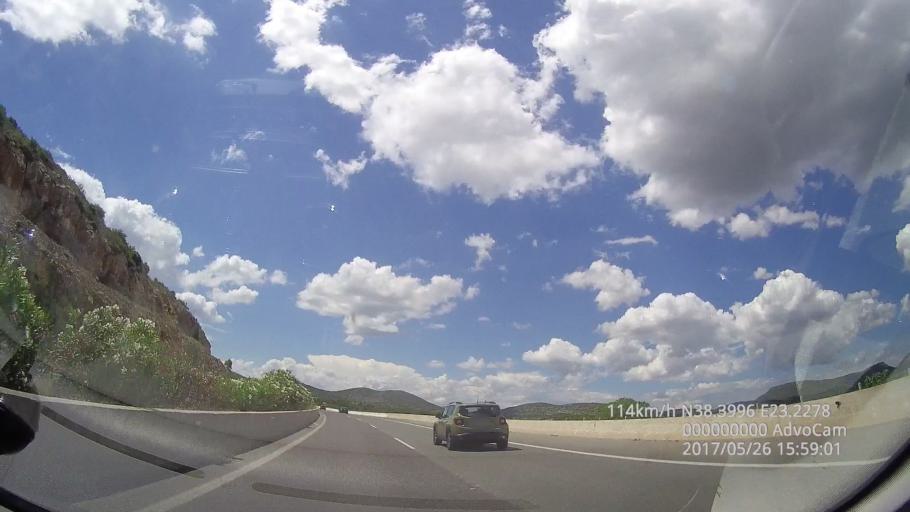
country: GR
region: Central Greece
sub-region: Nomos Fthiotidos
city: Ayios Konstandinos
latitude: 38.7615
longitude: 22.8424
